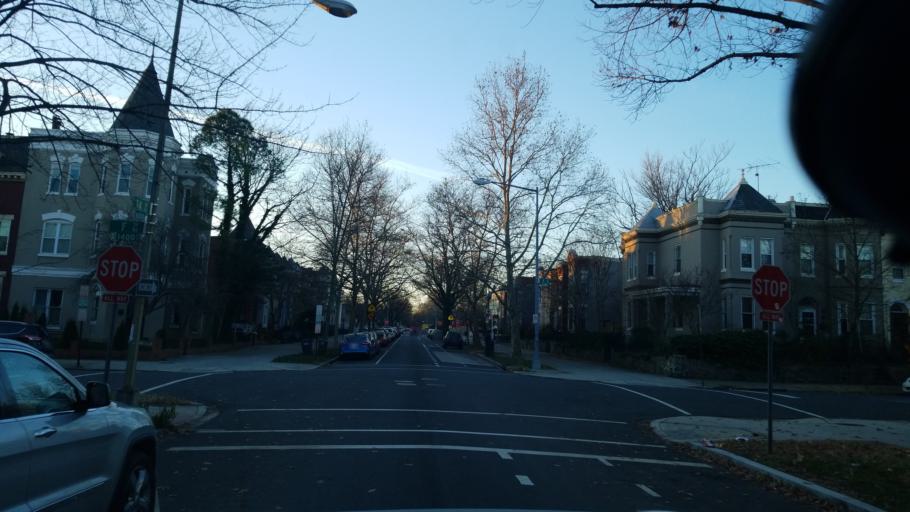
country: US
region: Maryland
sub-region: Prince George's County
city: Mount Rainier
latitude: 38.8975
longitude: -76.9855
